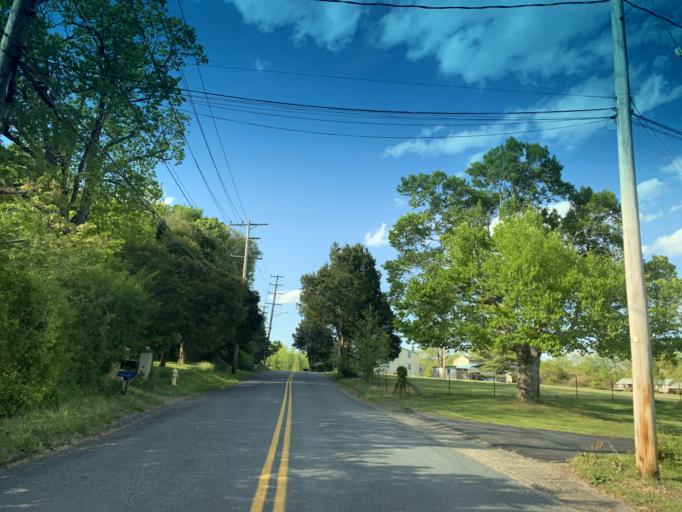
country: US
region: Maryland
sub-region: Harford County
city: Joppatowne
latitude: 39.4376
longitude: -76.3324
